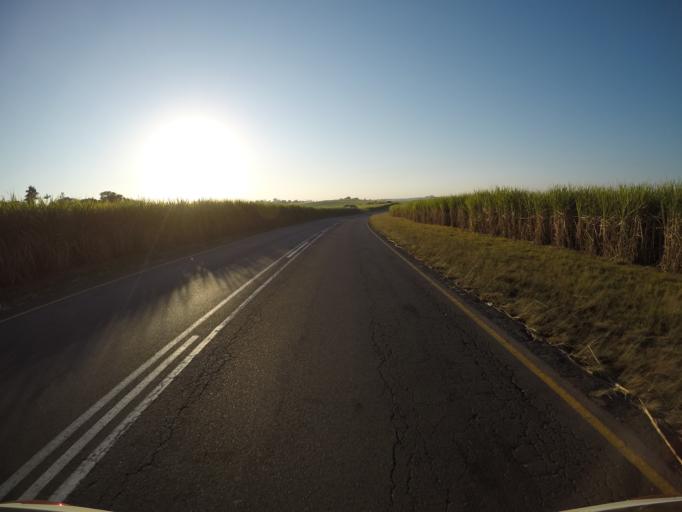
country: ZA
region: KwaZulu-Natal
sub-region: uThungulu District Municipality
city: eSikhawini
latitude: -28.9490
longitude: 31.6992
